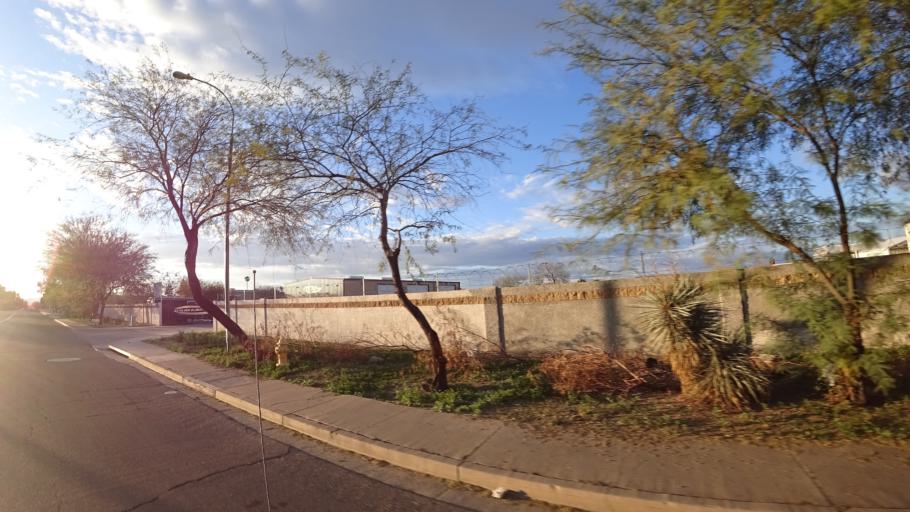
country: US
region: Arizona
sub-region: Maricopa County
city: Glendale
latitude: 33.5455
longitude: -112.2048
